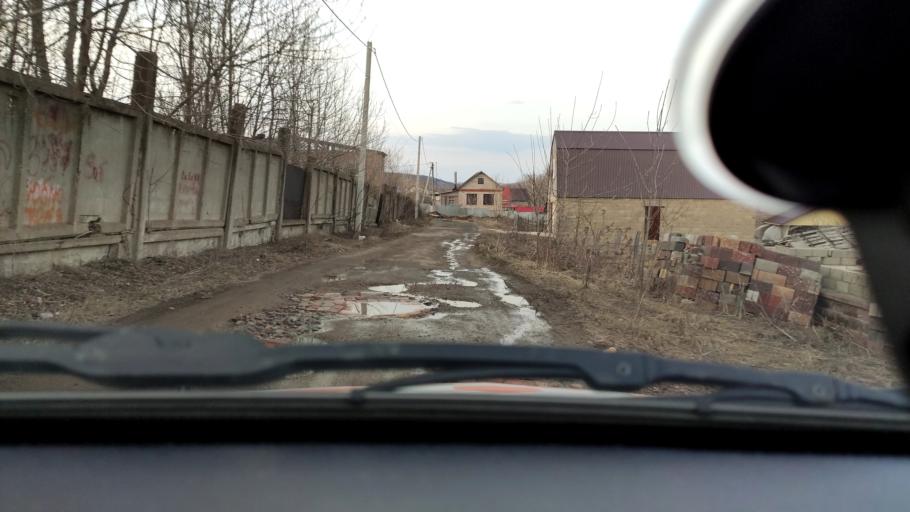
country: RU
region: Bashkortostan
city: Ufa
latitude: 54.8338
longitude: 56.1519
